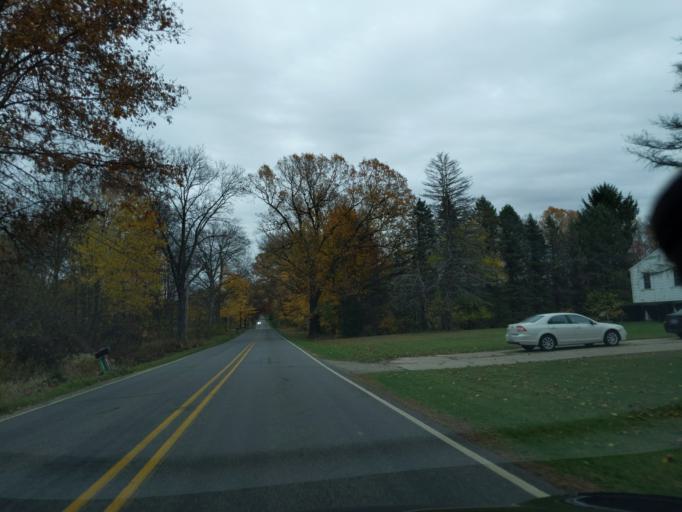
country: US
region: Michigan
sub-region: Jackson County
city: Spring Arbor
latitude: 42.2767
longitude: -84.5682
